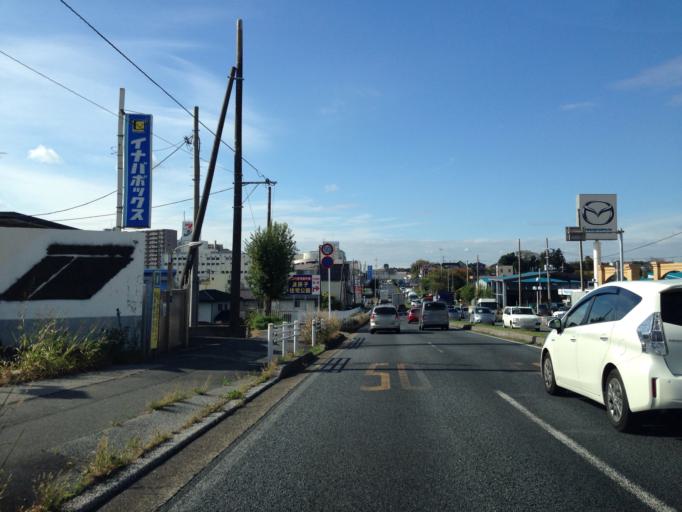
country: JP
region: Chiba
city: Abiko
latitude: 35.8769
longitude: 140.0138
